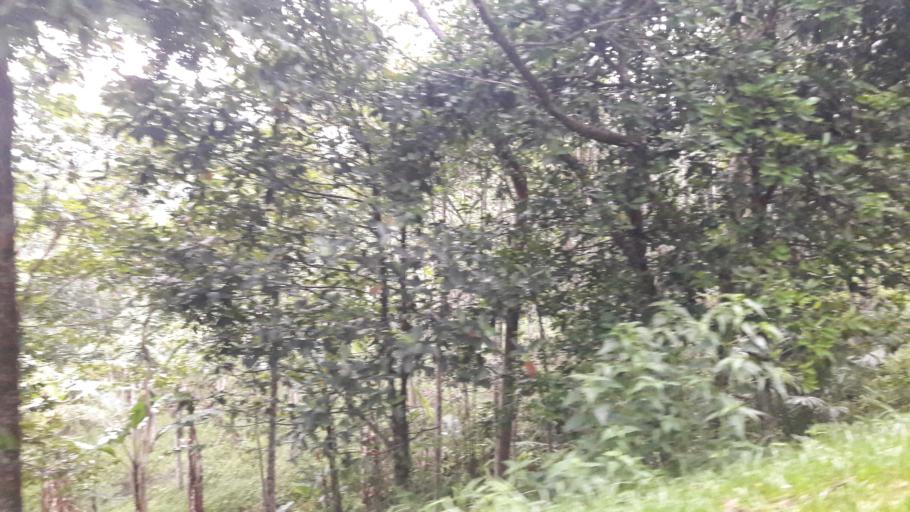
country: ID
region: West Java
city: Cipeundeuy
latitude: -6.6795
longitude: 106.5222
